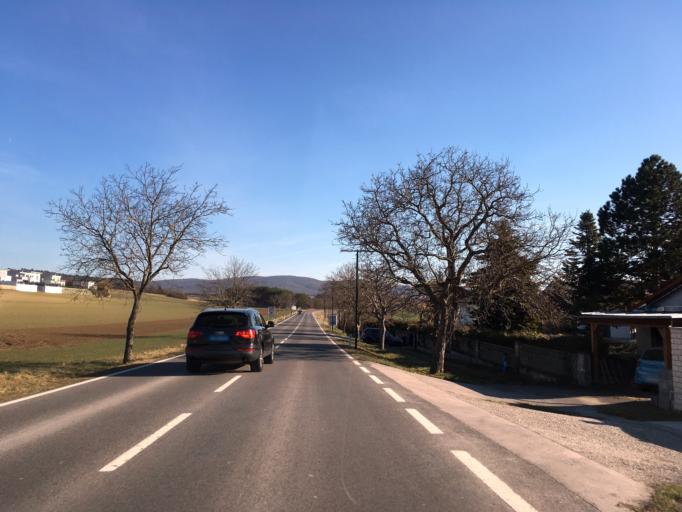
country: AT
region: Burgenland
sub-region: Eisenstadt-Umgebung
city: Wimpassing an der Leitha
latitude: 47.9118
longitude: 16.4291
